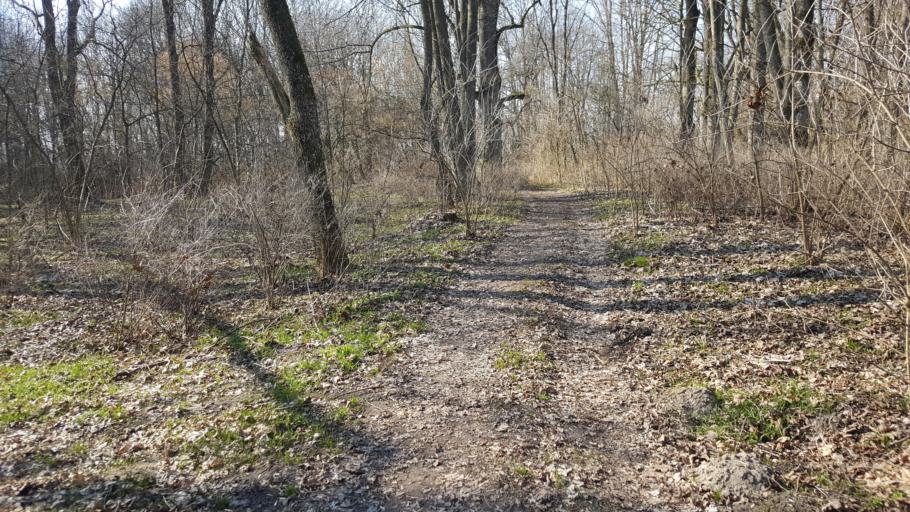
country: BY
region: Brest
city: Zhabinka
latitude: 52.3151
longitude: 23.9282
